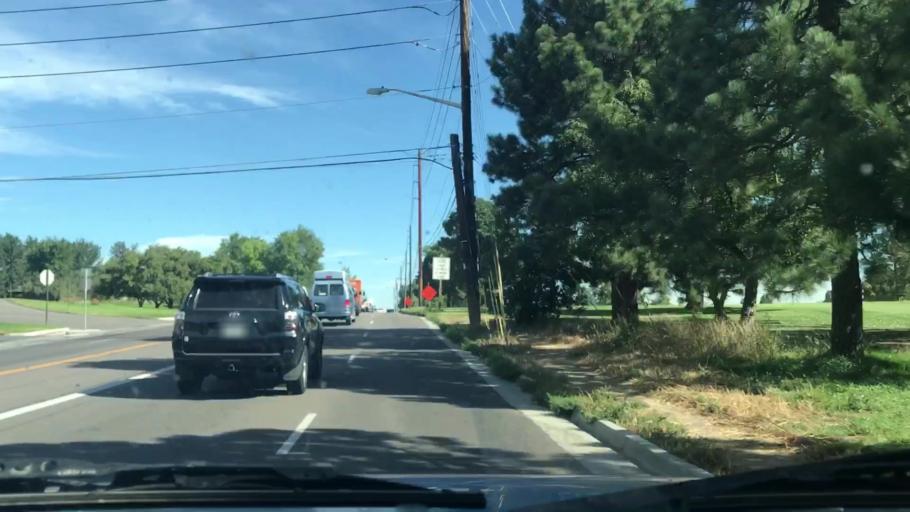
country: US
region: Colorado
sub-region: Jefferson County
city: Wheat Ridge
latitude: 39.7853
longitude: -105.0532
